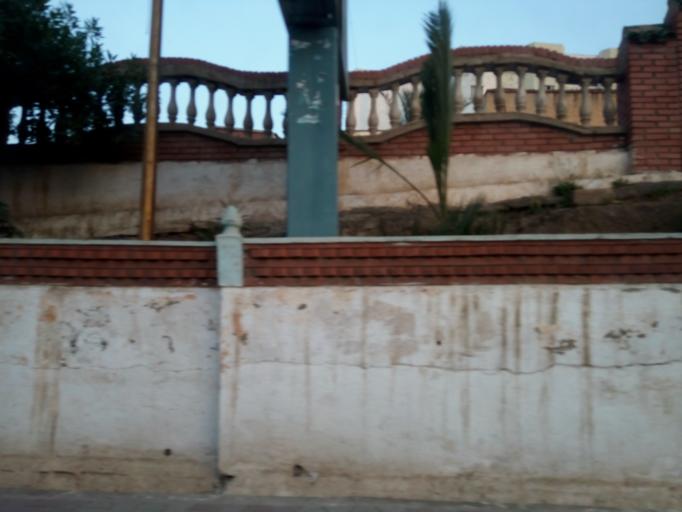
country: DZ
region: Tipaza
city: Bou Ismail
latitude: 36.6234
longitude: 2.6550
